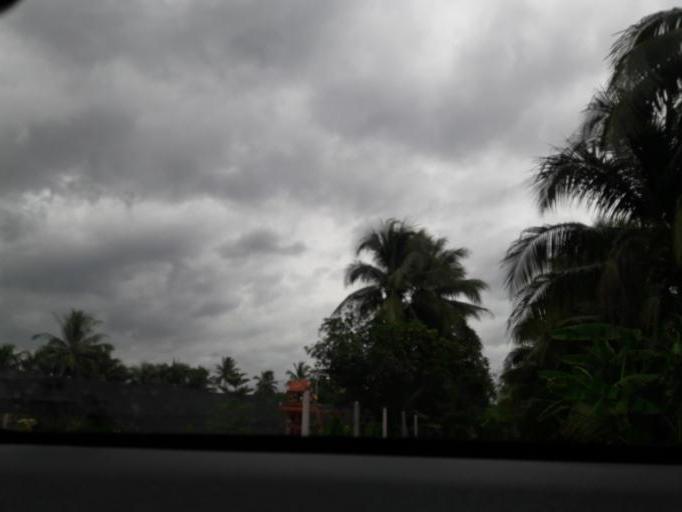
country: TH
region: Ratchaburi
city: Damnoen Saduak
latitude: 13.5713
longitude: 99.9947
